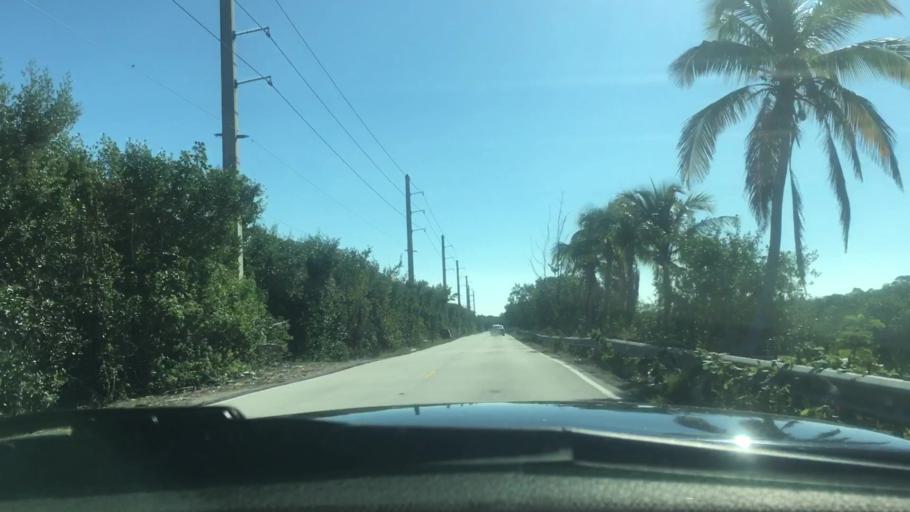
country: US
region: Florida
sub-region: Monroe County
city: North Key Largo
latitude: 25.2957
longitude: -80.3844
